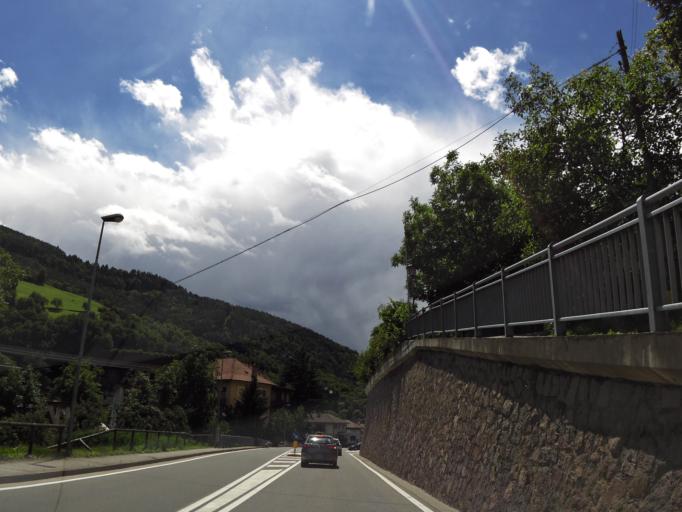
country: IT
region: Trentino-Alto Adige
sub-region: Bolzano
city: Chiusa
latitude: 46.6396
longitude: 11.5623
